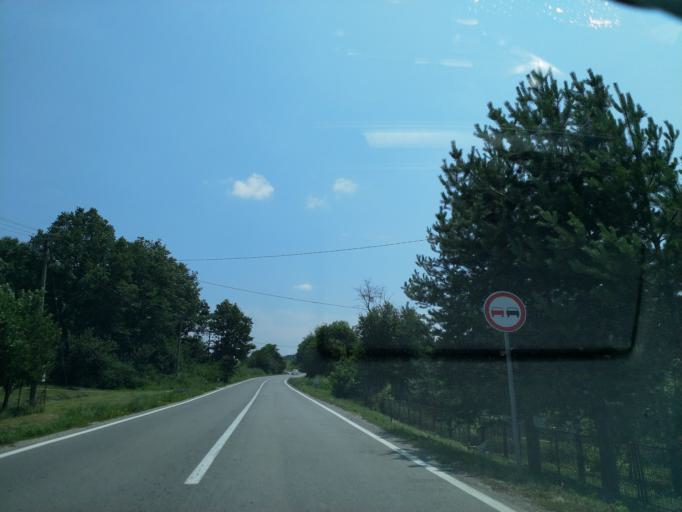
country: RS
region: Central Serbia
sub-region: Toplicki Okrug
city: Blace
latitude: 43.3135
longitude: 21.2458
